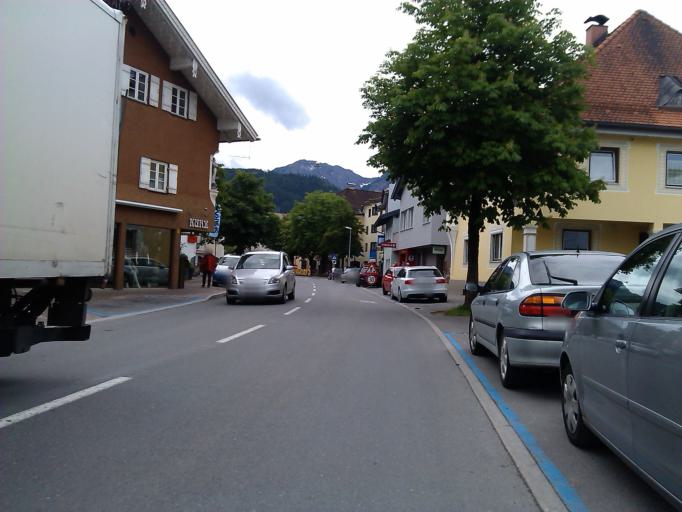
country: AT
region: Tyrol
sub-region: Politischer Bezirk Reutte
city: Reutte
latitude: 47.4872
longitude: 10.7194
